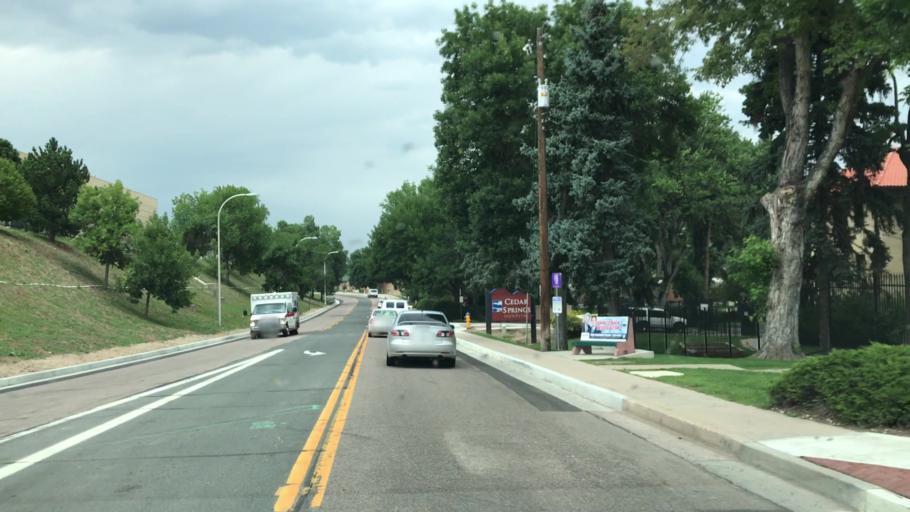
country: US
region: Colorado
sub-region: El Paso County
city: Colorado Springs
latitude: 38.8008
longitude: -104.8176
